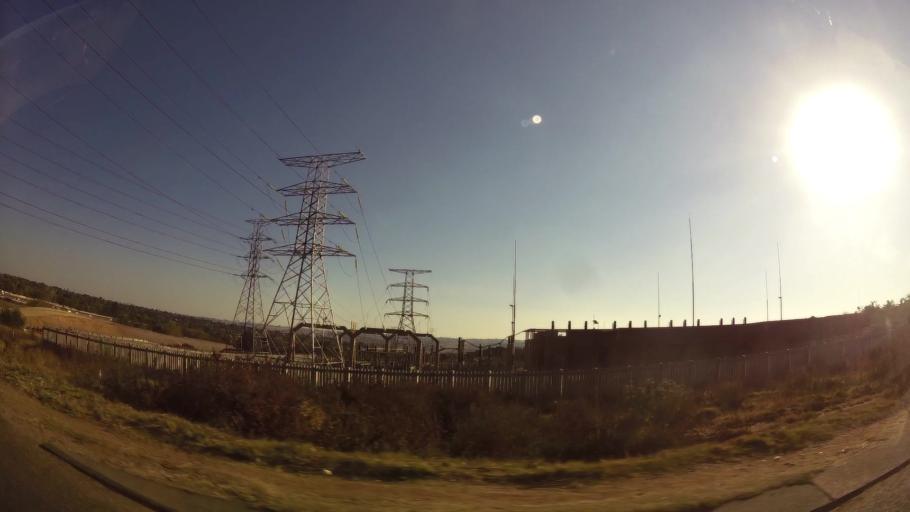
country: ZA
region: Gauteng
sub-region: City of Tshwane Metropolitan Municipality
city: Centurion
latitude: -25.8856
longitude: 28.1415
